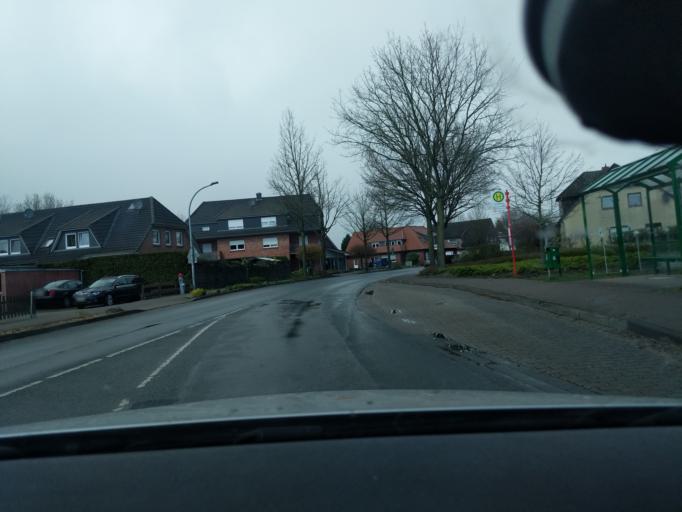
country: DE
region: Lower Saxony
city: Ahlerstedt
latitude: 53.4007
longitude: 9.4486
